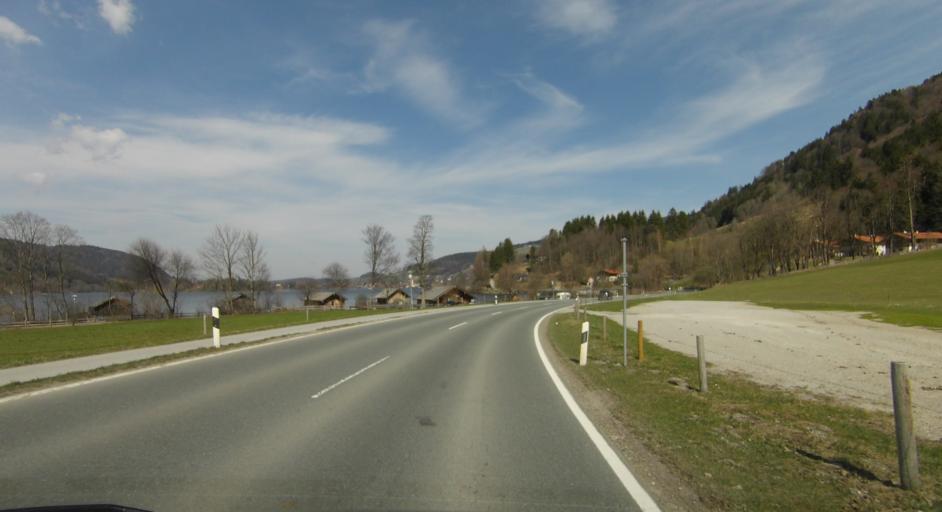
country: DE
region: Bavaria
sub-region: Upper Bavaria
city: Schliersee
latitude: 47.7122
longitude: 11.8696
